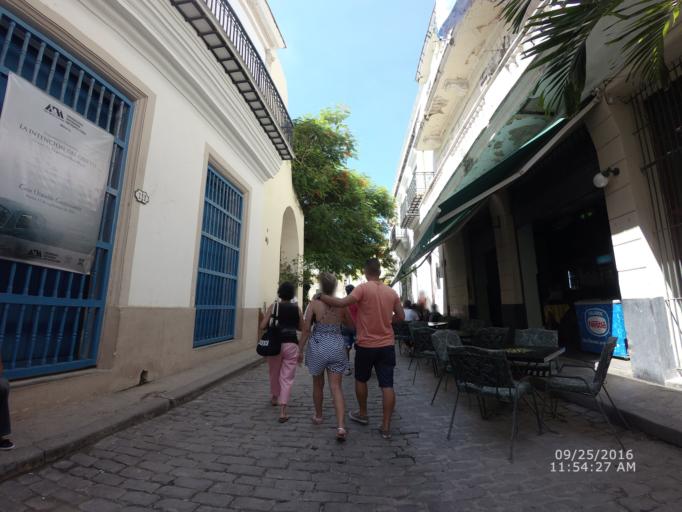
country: CU
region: La Habana
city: La Habana Vieja
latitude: 23.1387
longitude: -82.3494
